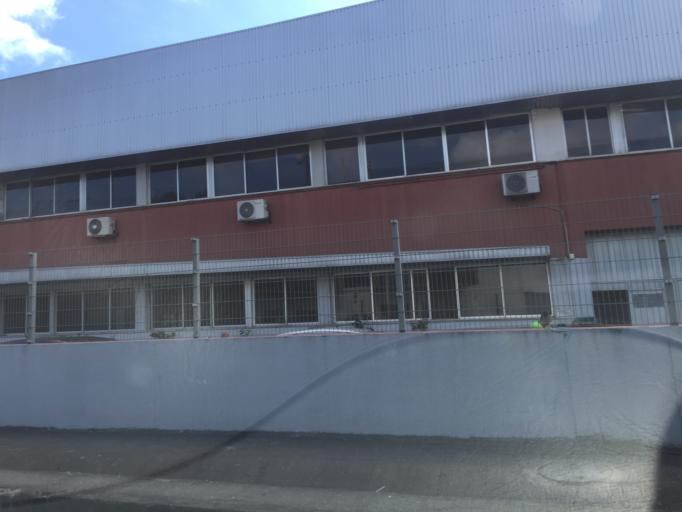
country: PT
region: Lisbon
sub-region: Odivelas
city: Povoa de Santo Adriao
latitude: 38.8044
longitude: -9.1576
